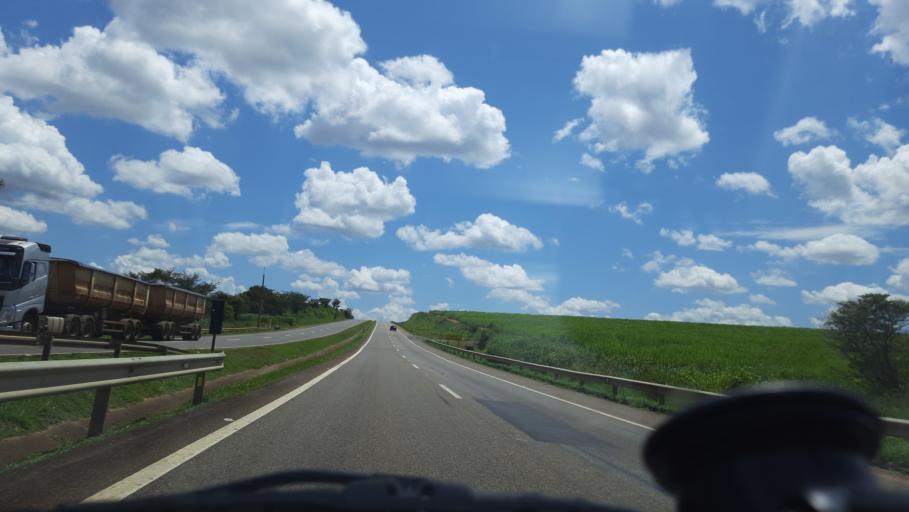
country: BR
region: Sao Paulo
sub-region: Aguai
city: Aguai
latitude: -21.9877
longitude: -47.0399
